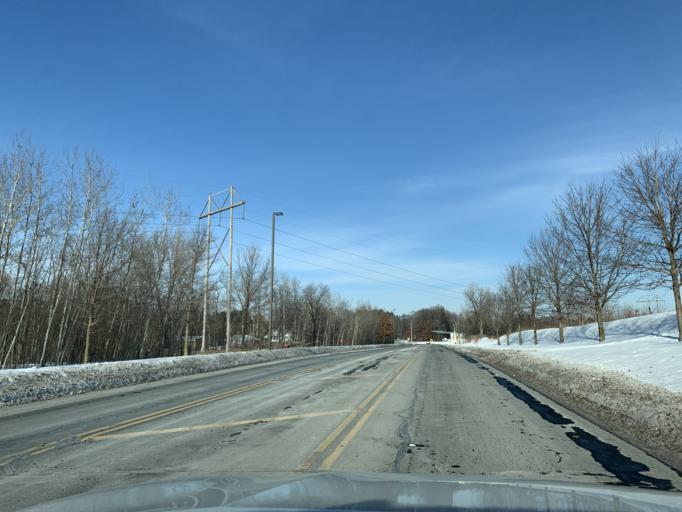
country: US
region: Minnesota
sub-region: Anoka County
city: Columbus
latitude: 45.2481
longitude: -93.0349
